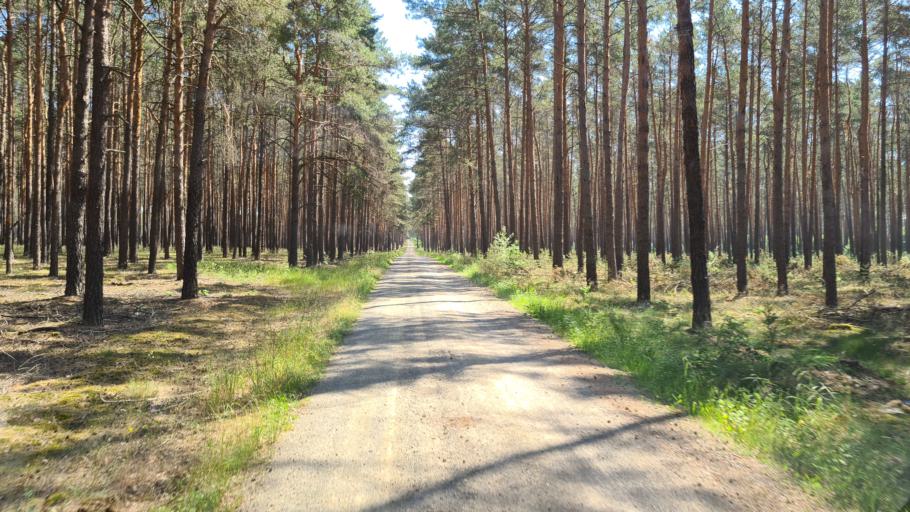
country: DE
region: Brandenburg
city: Schlieben
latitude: 51.7798
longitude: 13.3535
